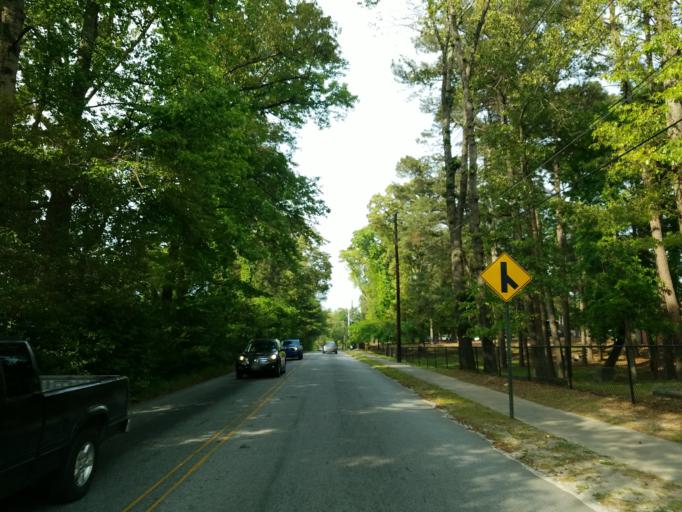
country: US
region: Georgia
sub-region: Cobb County
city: Vinings
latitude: 33.7908
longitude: -84.4952
